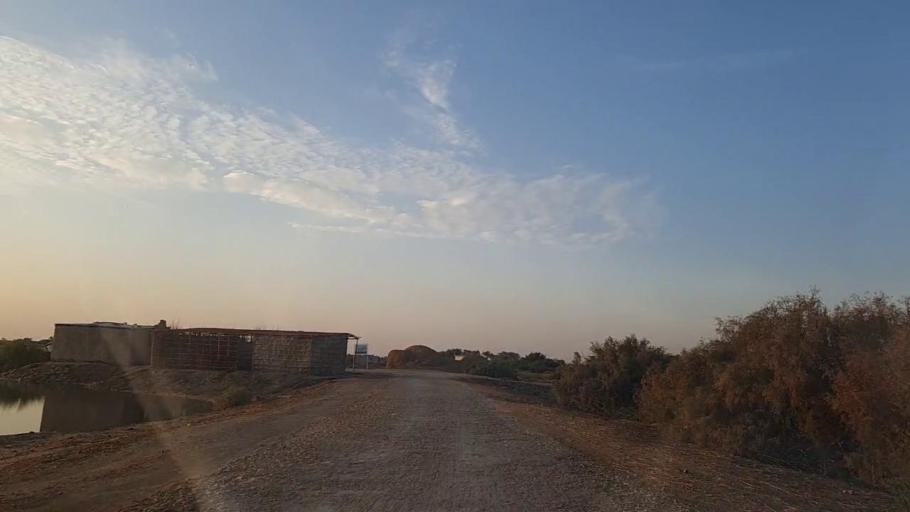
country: PK
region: Sindh
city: Chuhar Jamali
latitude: 24.4558
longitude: 68.1168
